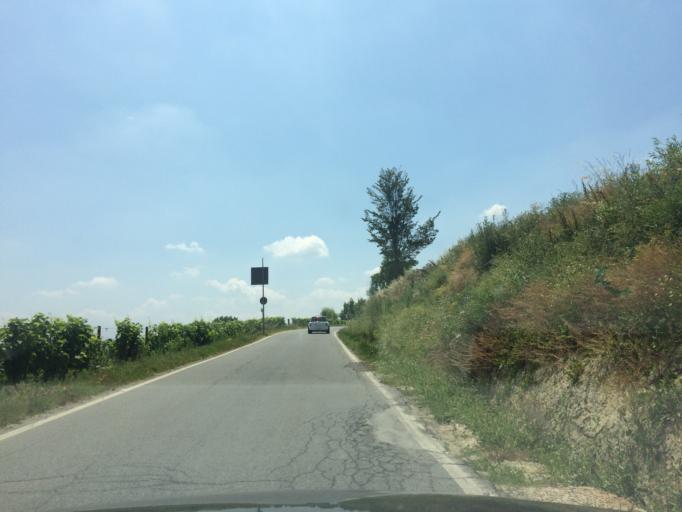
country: IT
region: Piedmont
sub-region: Provincia di Asti
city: Calosso
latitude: 44.7435
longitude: 8.2291
